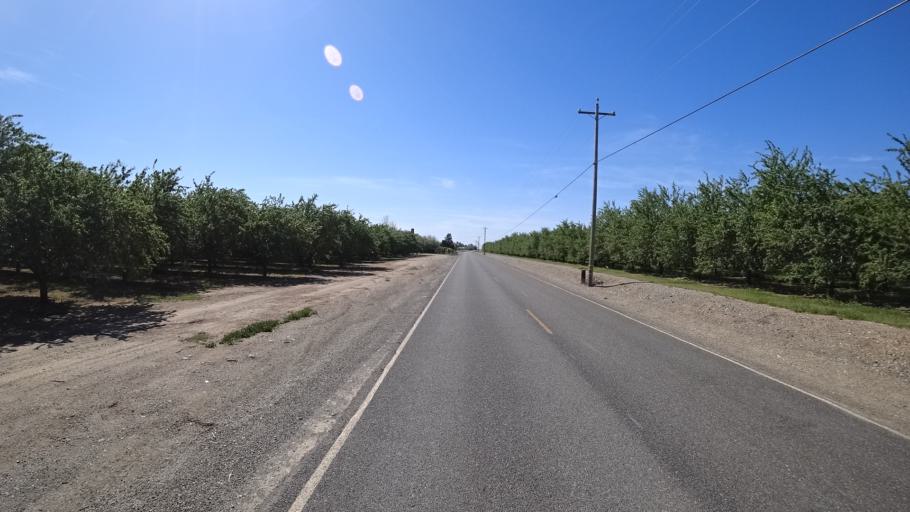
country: US
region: California
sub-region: Glenn County
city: Hamilton City
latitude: 39.6988
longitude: -122.1034
